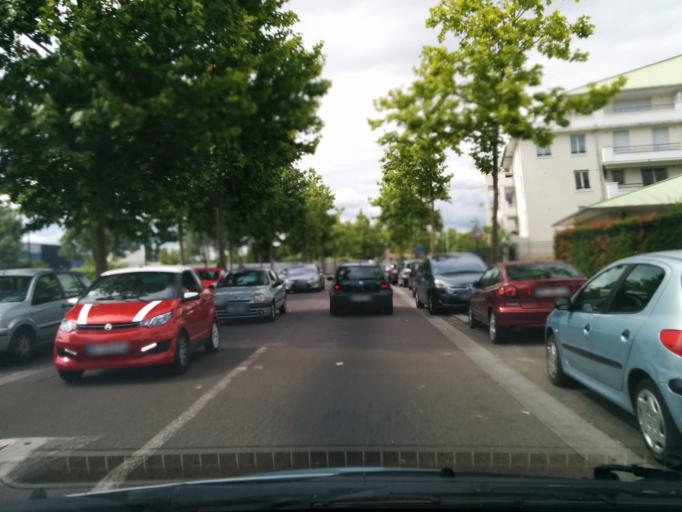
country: FR
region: Ile-de-France
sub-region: Departement des Yvelines
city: Mantes-la-Jolie
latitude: 48.9975
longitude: 1.7142
